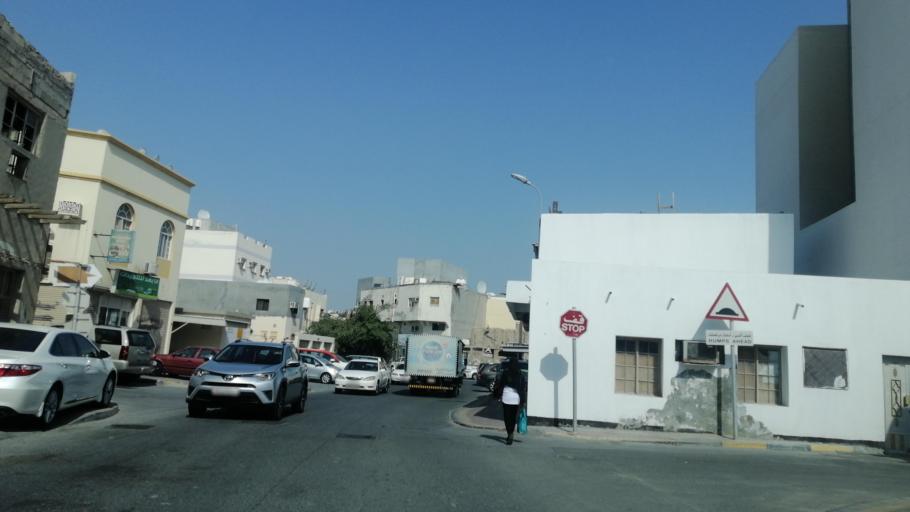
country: BH
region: Muharraq
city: Al Muharraq
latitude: 26.2534
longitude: 50.6312
